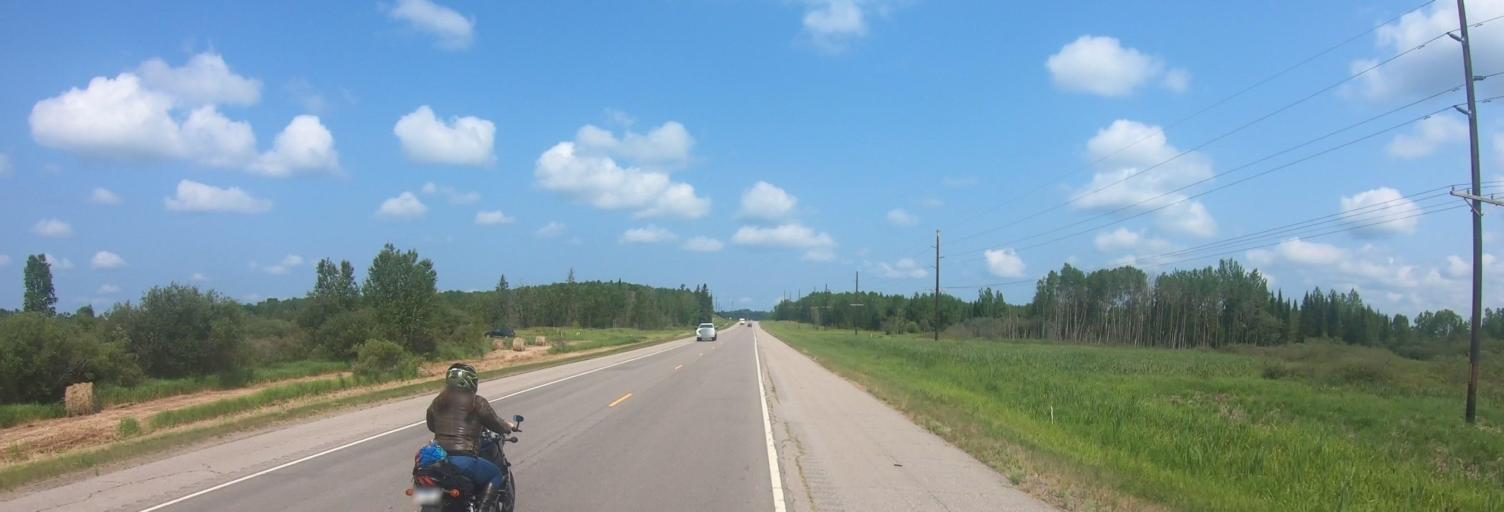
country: US
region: Minnesota
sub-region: Saint Louis County
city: Chisholm
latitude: 47.9486
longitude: -92.8289
